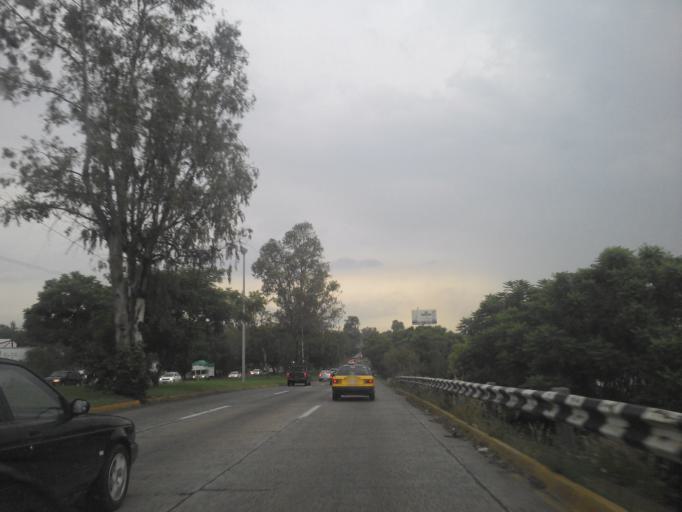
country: MX
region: Jalisco
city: Tlaquepaque
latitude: 20.6306
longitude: -103.3356
